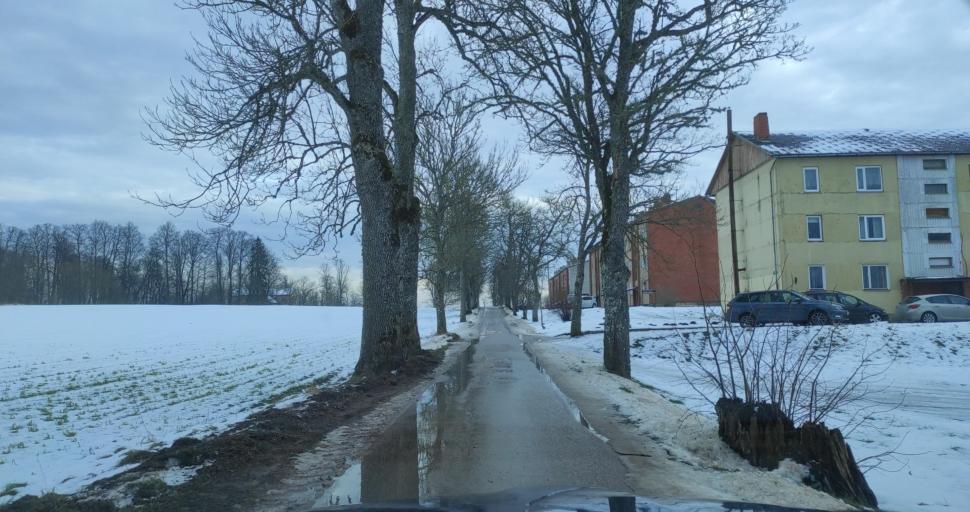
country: LV
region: Kuldigas Rajons
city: Kuldiga
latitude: 57.0188
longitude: 21.9040
